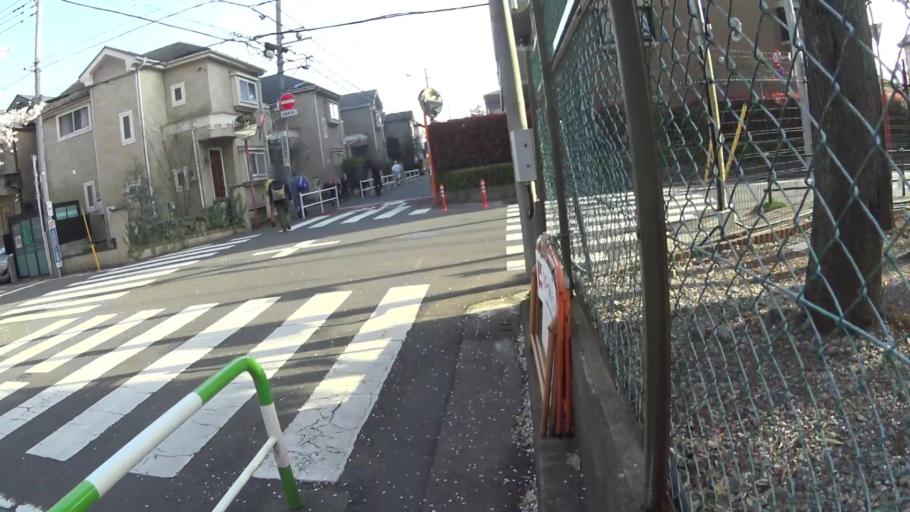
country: JP
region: Tokyo
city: Kokubunji
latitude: 35.7155
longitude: 139.5022
